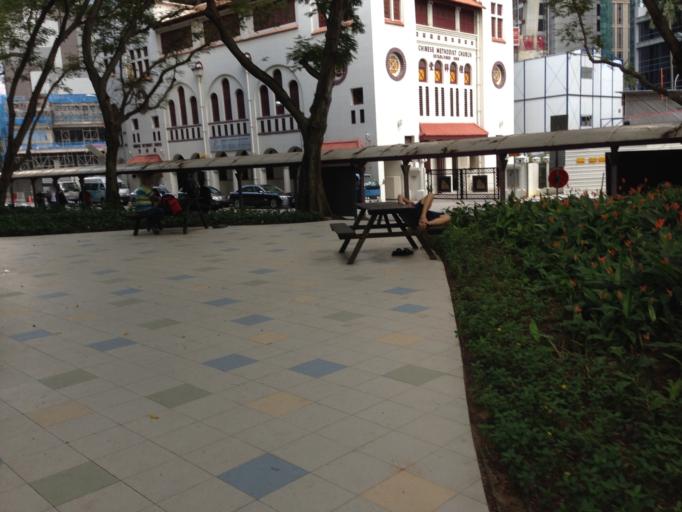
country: SG
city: Singapore
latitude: 1.2781
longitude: 103.8465
